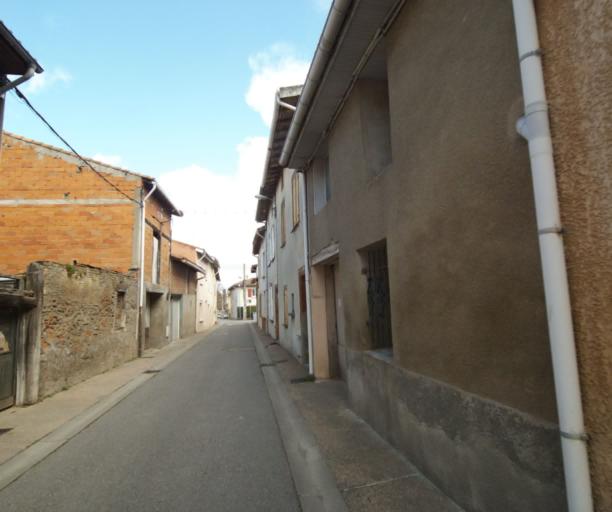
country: FR
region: Midi-Pyrenees
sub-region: Departement de l'Ariege
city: Saverdun
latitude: 43.2290
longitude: 1.5771
